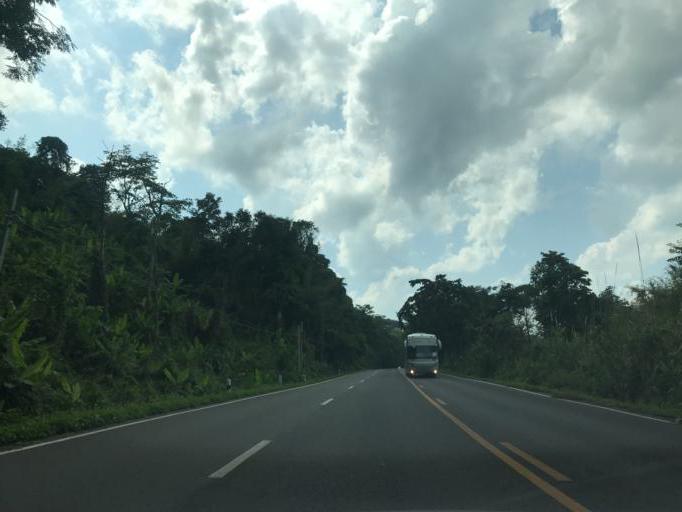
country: TH
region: Phayao
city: Phayao
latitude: 19.0576
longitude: 99.7866
